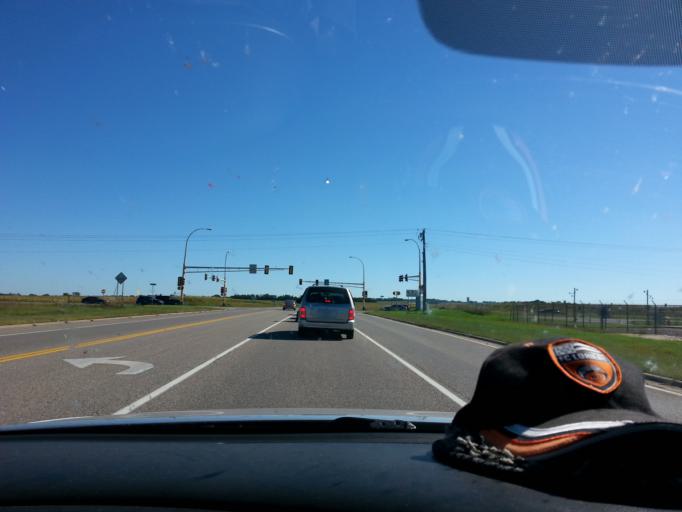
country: US
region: Minnesota
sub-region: Dakota County
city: Rosemount
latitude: 44.7180
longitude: -93.1293
